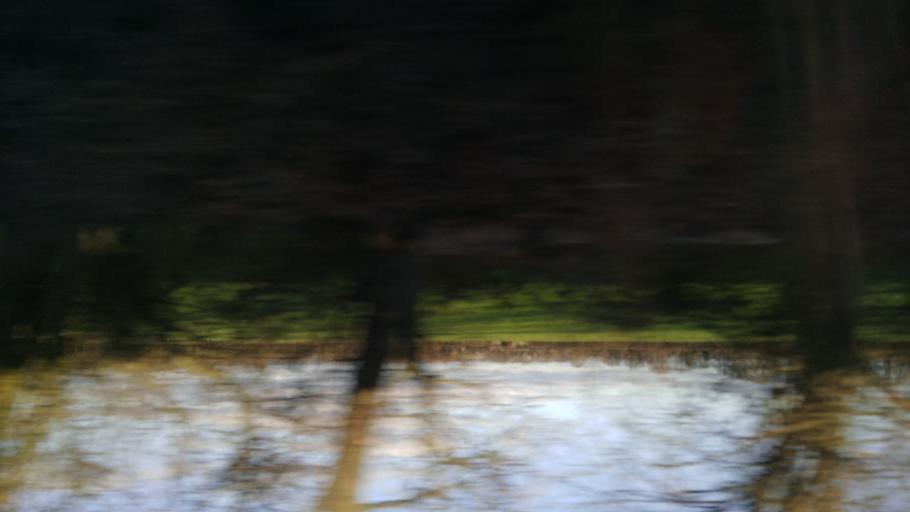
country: GB
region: England
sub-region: Kent
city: Yalding
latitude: 51.1790
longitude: 0.4410
